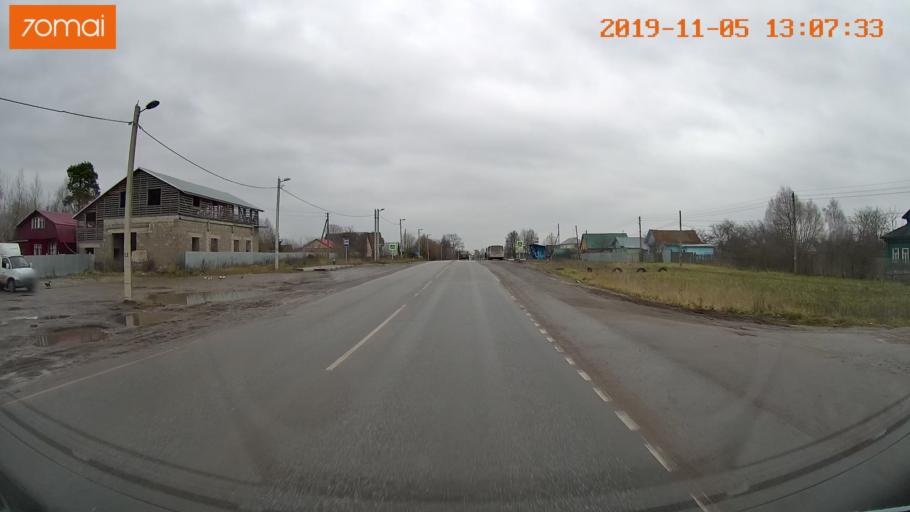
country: RU
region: Ivanovo
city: Kitovo
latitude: 56.8673
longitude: 41.2820
